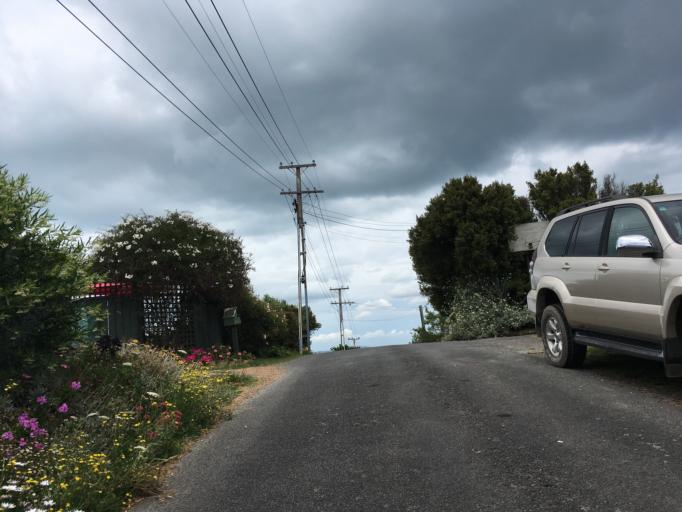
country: NZ
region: Auckland
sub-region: Auckland
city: Pakuranga
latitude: -36.7894
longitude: 175.0206
